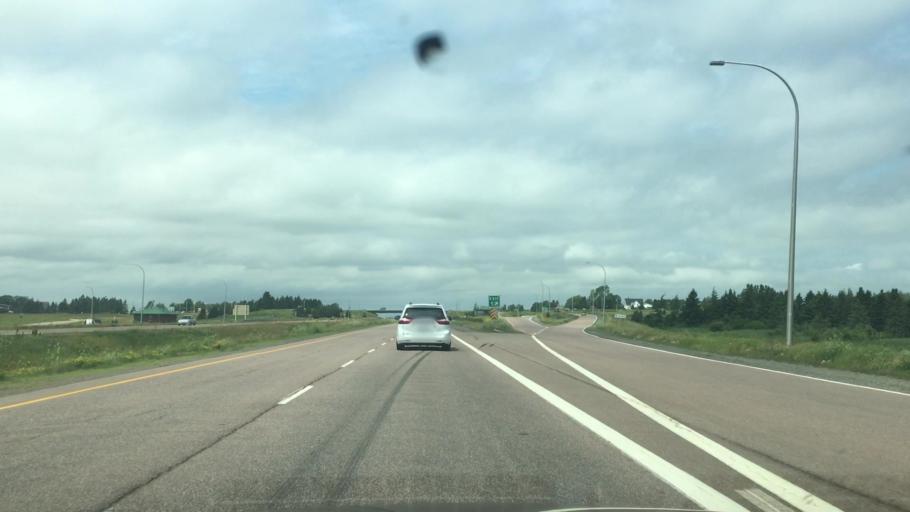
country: CA
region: Nova Scotia
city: Amherst
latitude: 45.8497
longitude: -64.2476
